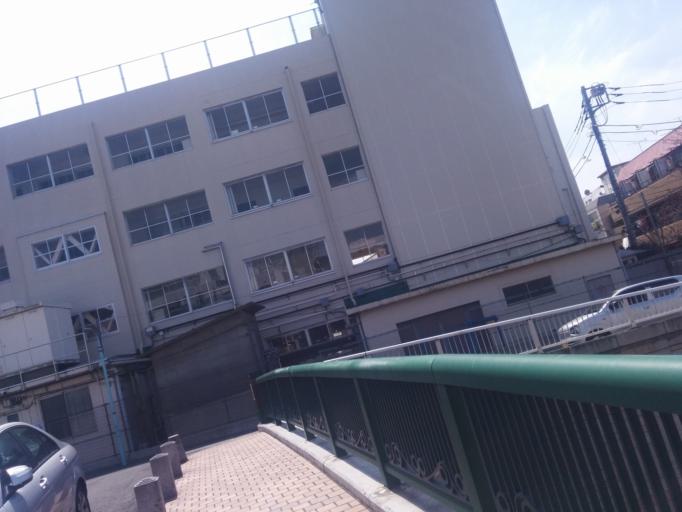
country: JP
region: Tokyo
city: Tokyo
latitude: 35.6925
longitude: 139.6795
